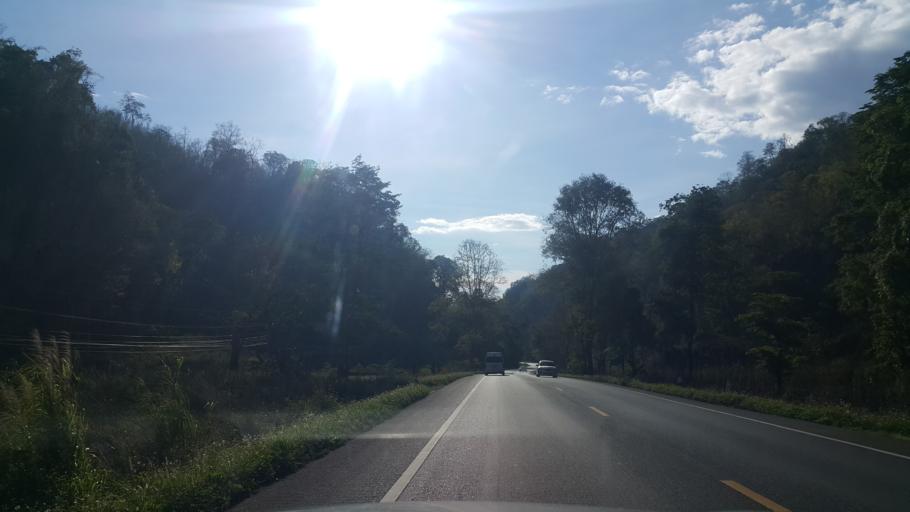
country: TH
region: Lampang
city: Wang Nuea
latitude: 19.0637
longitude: 99.7486
